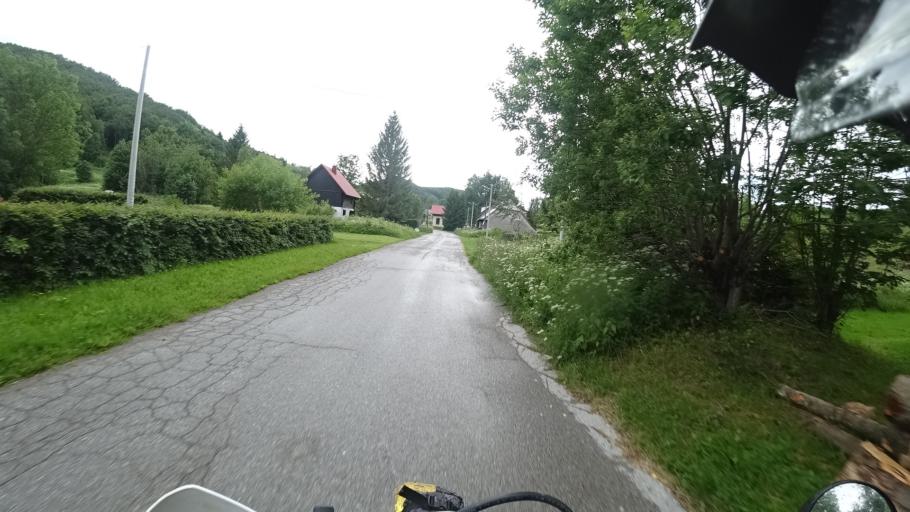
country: HR
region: Primorsko-Goranska
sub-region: Grad Delnice
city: Delnice
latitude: 45.3044
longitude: 14.9072
